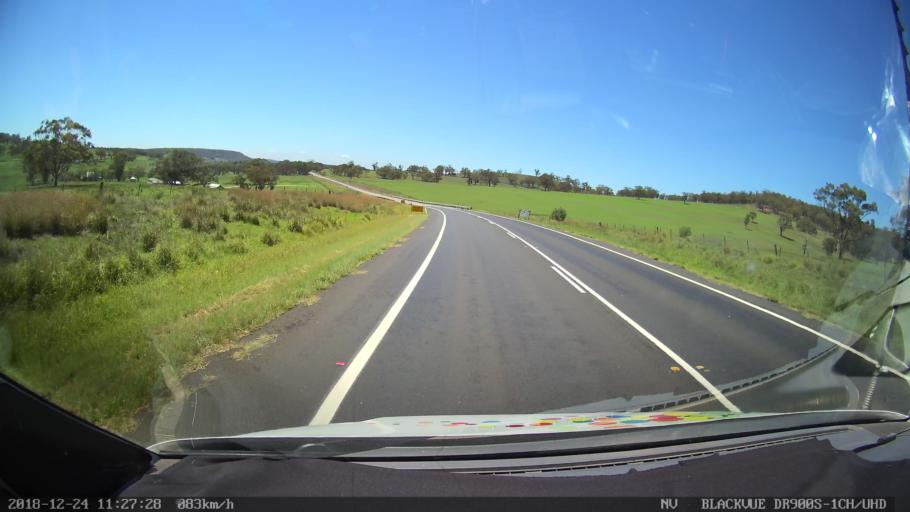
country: AU
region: New South Wales
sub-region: Upper Hunter Shire
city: Merriwa
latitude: -32.1823
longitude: 150.4353
